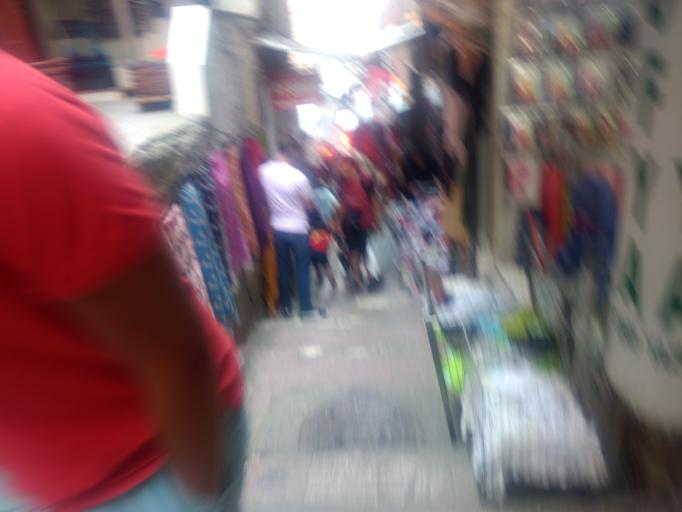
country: TR
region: Istanbul
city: Eminoenue
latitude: 41.0123
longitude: 28.9699
